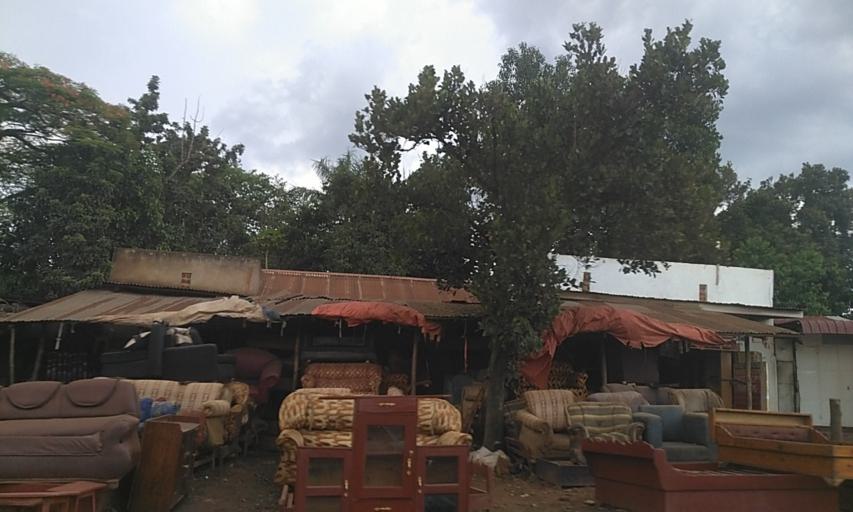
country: UG
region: Central Region
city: Kampala Central Division
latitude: 0.3193
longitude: 32.5079
